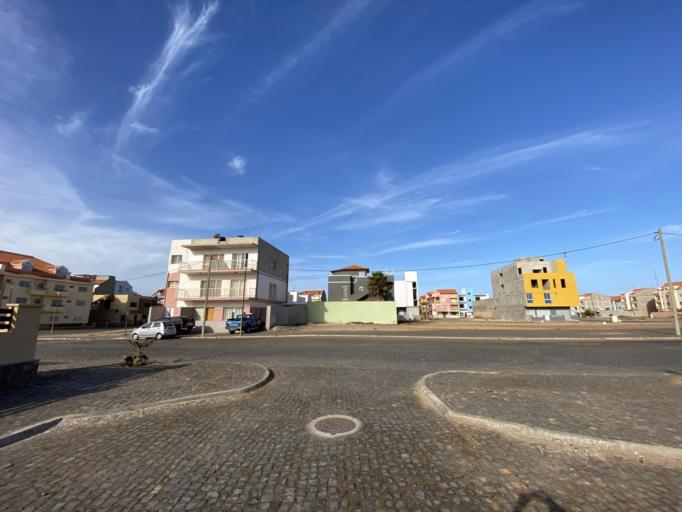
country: CV
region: Sal
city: Santa Maria
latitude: 16.5987
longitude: -22.8983
